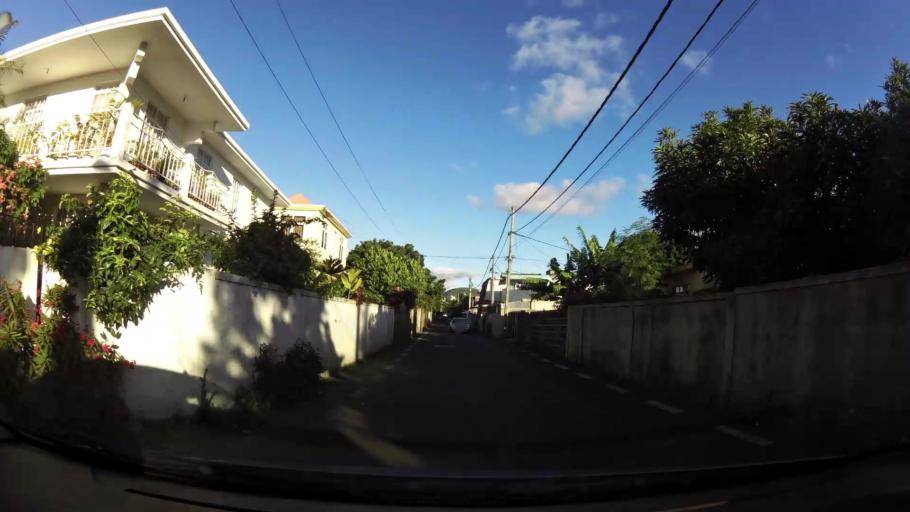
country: MU
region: Plaines Wilhems
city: Quatre Bornes
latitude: -20.2472
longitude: 57.4685
